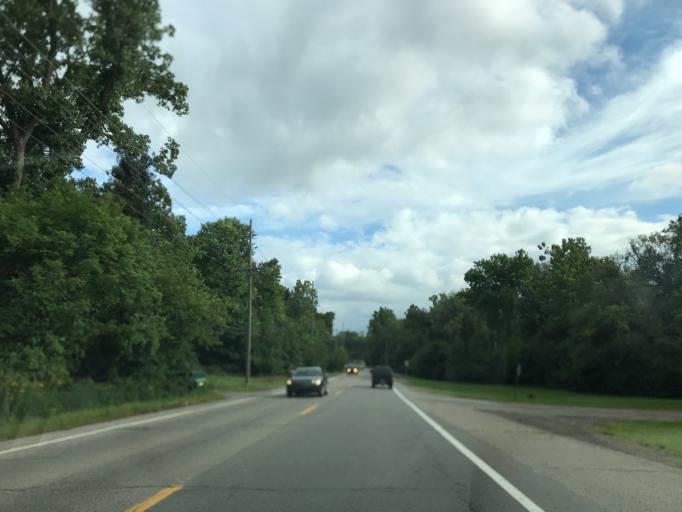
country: US
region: Michigan
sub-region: Wayne County
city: Northville
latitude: 42.4036
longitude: -83.4693
